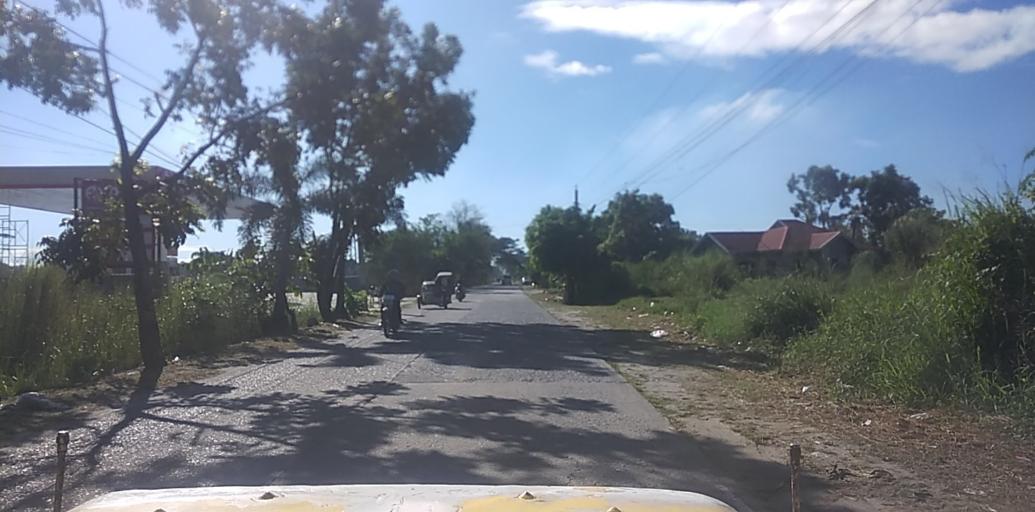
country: PH
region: Central Luzon
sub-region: Province of Pampanga
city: Mexico
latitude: 15.0780
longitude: 120.7180
